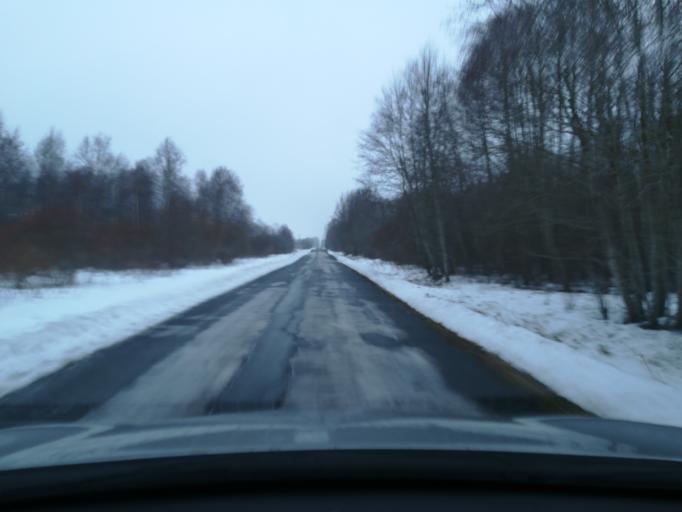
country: EE
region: Harju
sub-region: Raasiku vald
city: Raasiku
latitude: 59.3413
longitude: 25.2277
